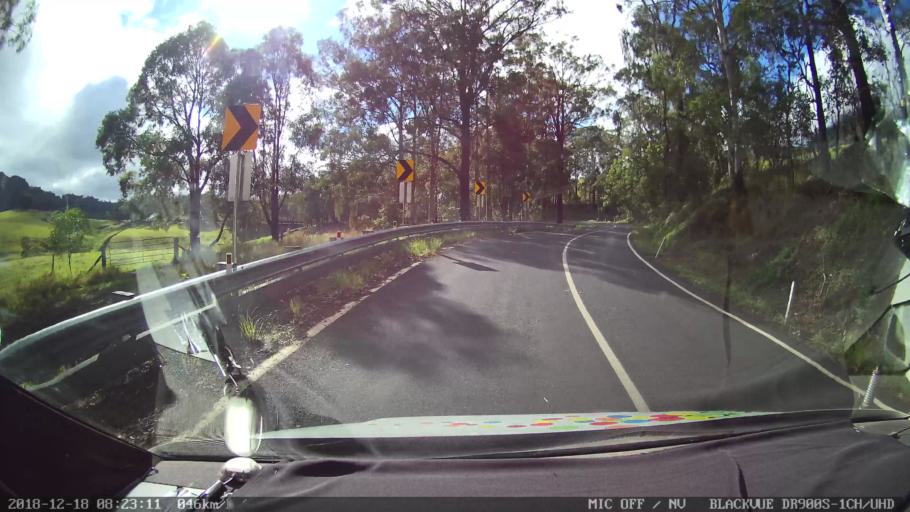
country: AU
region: New South Wales
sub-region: Kyogle
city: Kyogle
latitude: -28.3243
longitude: 152.7277
